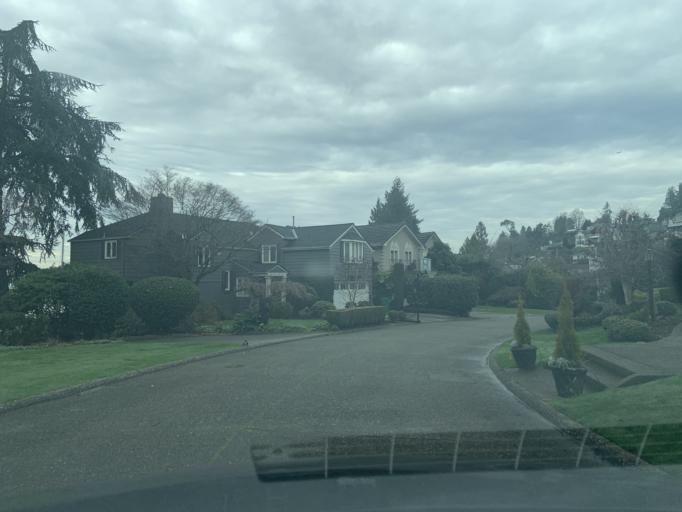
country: US
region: Washington
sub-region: King County
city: Yarrow Point
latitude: 47.6576
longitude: -122.2711
